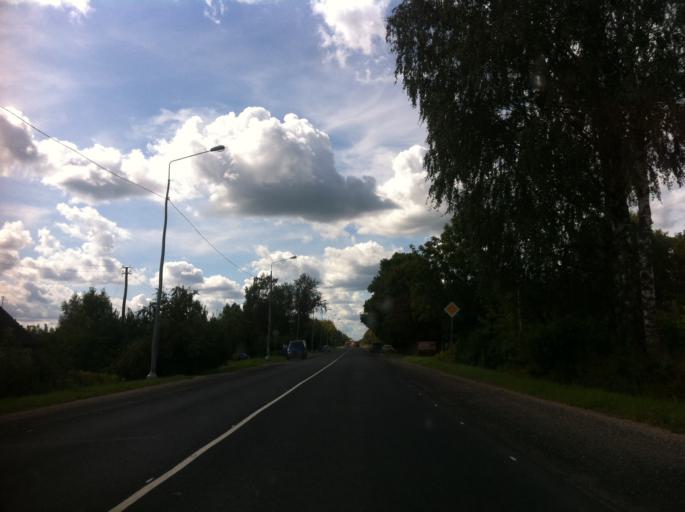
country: RU
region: Pskov
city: Izborsk
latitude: 57.7314
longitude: 27.9759
